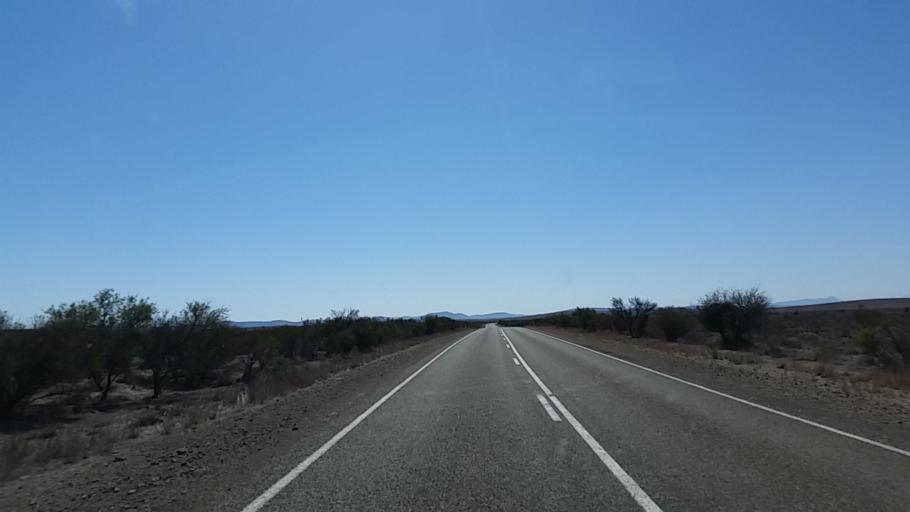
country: AU
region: South Australia
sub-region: Flinders Ranges
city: Quorn
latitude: -32.1277
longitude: 138.5107
